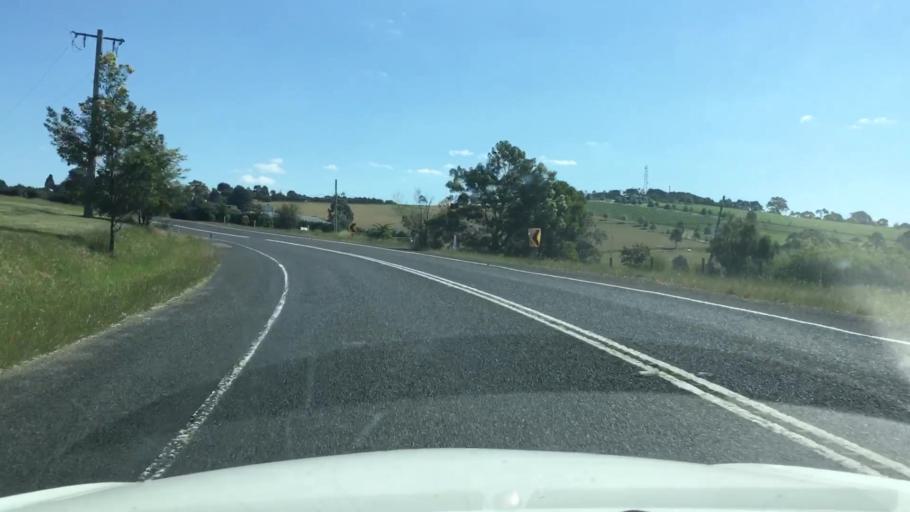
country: AU
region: Victoria
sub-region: Nillumbik
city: North Warrandyte
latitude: -37.6838
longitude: 145.2360
